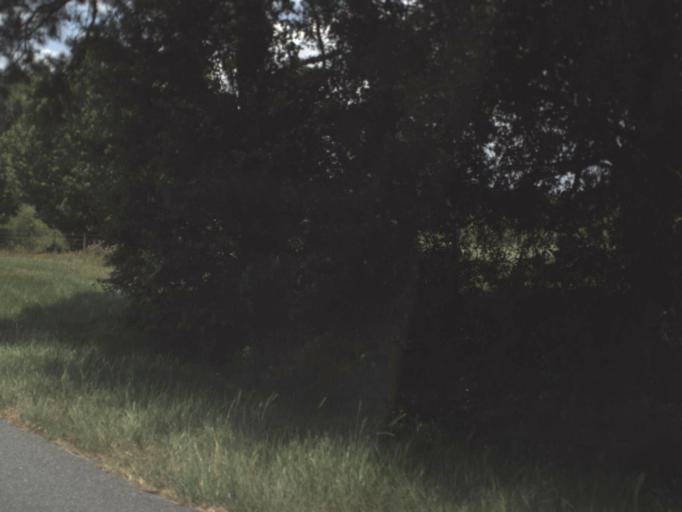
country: US
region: Florida
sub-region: Alachua County
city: High Springs
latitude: 30.0041
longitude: -82.5513
